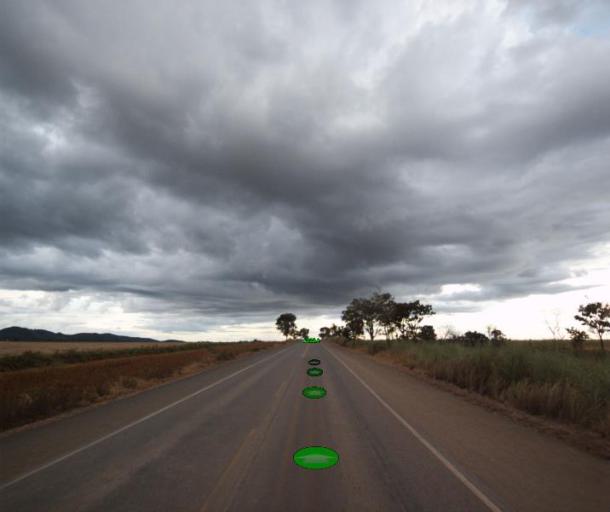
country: BR
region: Goias
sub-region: Uruacu
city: Uruacu
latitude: -14.7101
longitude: -49.2249
